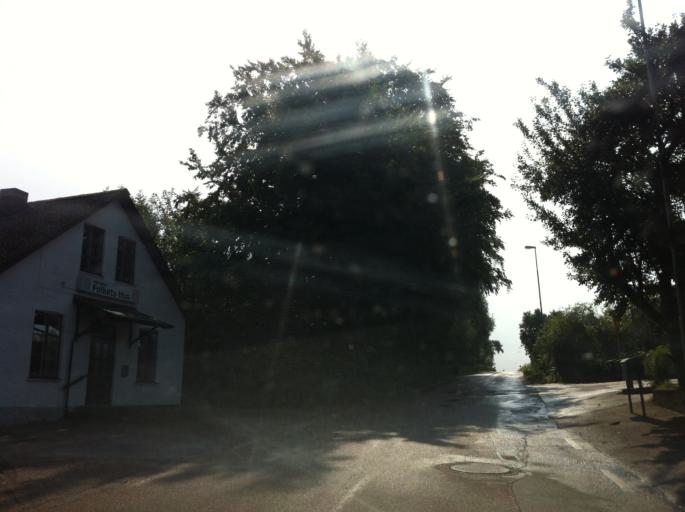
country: SE
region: Skane
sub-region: Helsingborg
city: Glumslov
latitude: 55.9303
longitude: 12.8741
